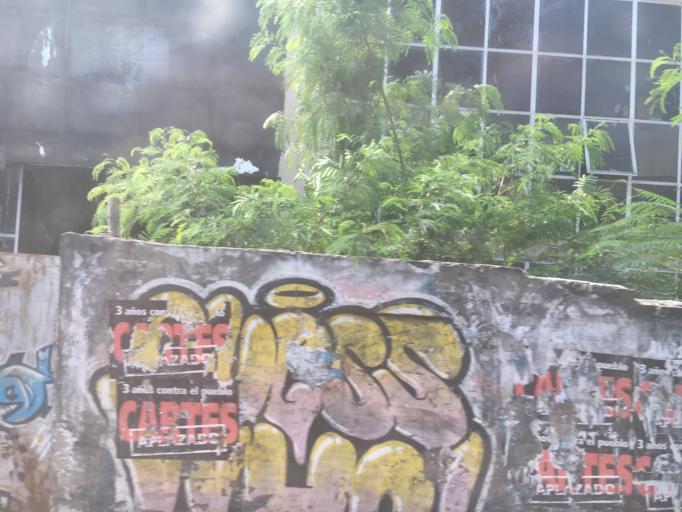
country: PY
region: Asuncion
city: Asuncion
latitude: -25.2882
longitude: -57.6285
